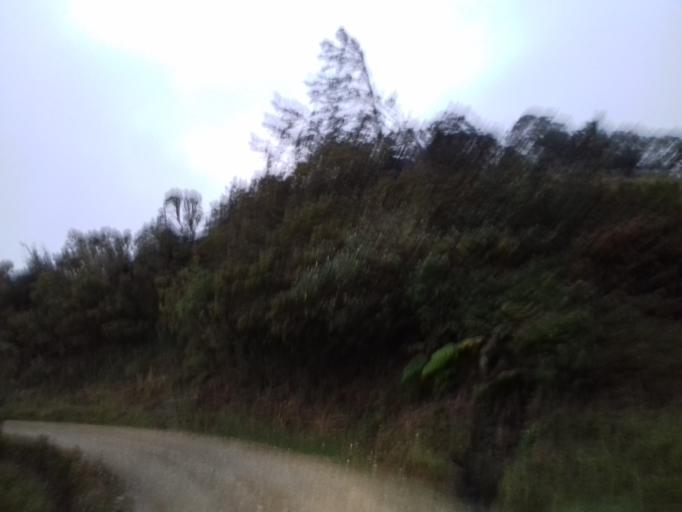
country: CO
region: Quindio
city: Salento
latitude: 4.5629
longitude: -75.5177
